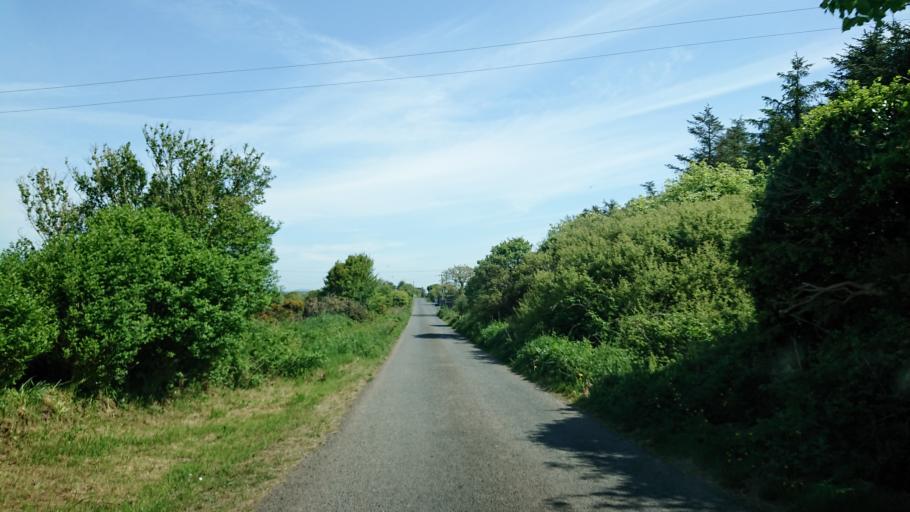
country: IE
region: Munster
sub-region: Waterford
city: Tra Mhor
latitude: 52.1486
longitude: -7.0790
